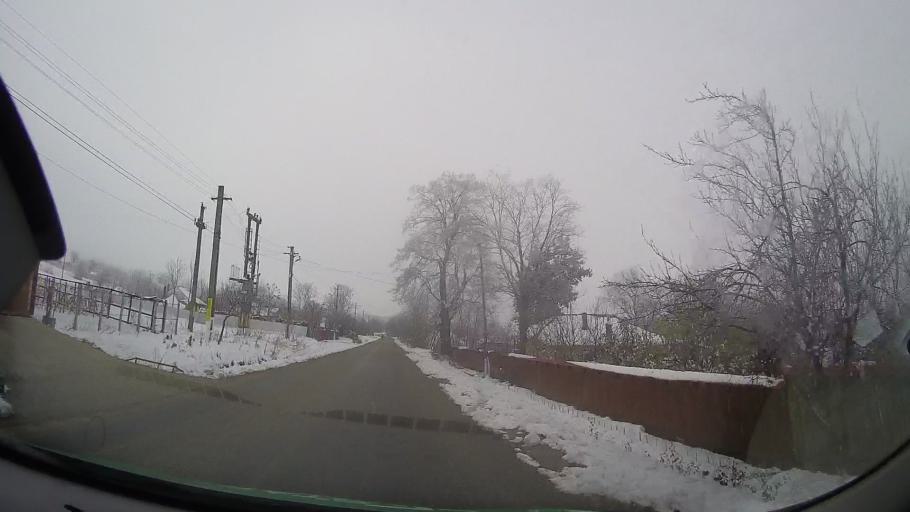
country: RO
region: Bacau
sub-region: Comuna Oncesti
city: Oncesti
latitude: 46.4435
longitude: 27.2657
